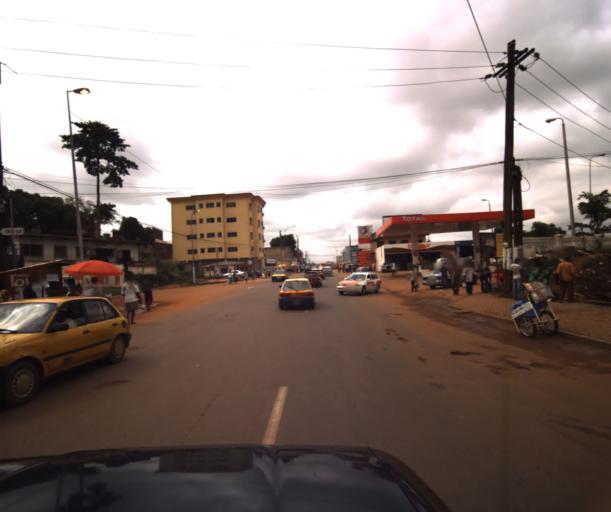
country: CM
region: Centre
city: Yaounde
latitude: 3.8581
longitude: 11.5220
